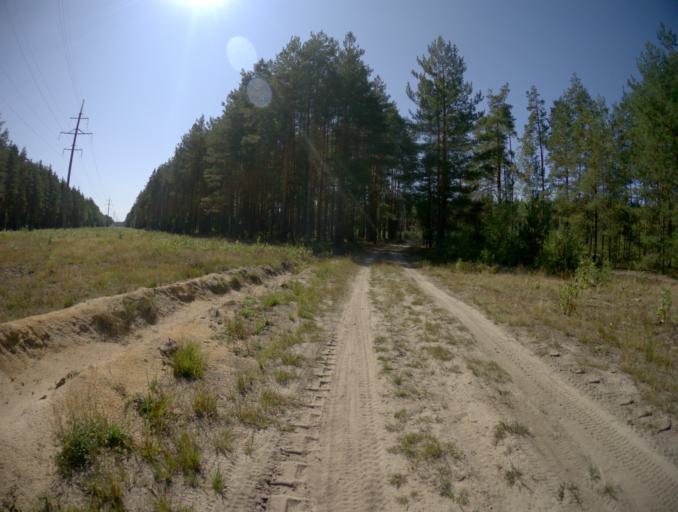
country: RU
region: Vladimir
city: Sobinka
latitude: 55.9534
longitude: 39.9942
